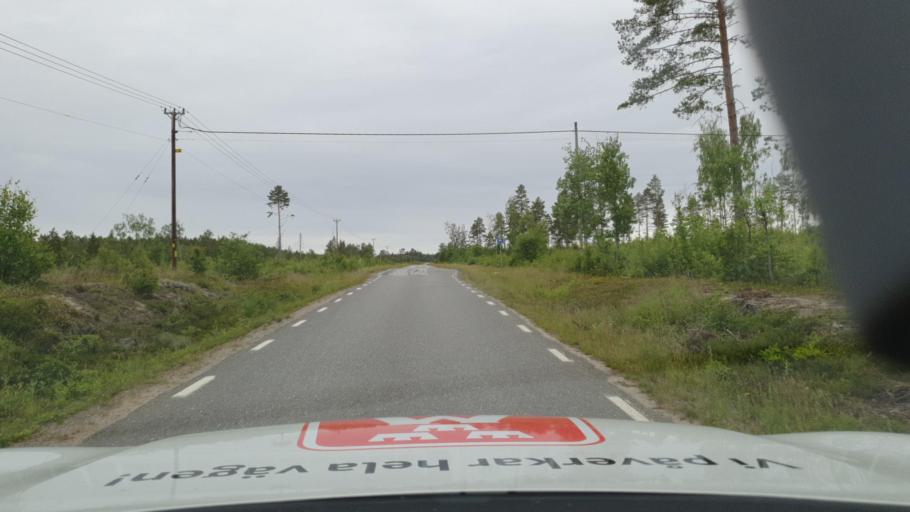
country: SE
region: Vaesterbotten
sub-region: Nordmalings Kommun
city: Nordmaling
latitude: 63.4541
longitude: 19.4674
